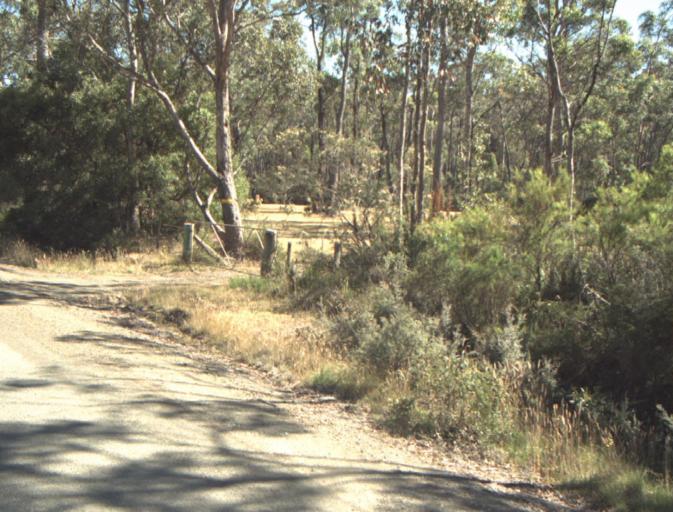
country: AU
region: Tasmania
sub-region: Launceston
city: Newstead
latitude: -41.3727
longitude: 147.2807
